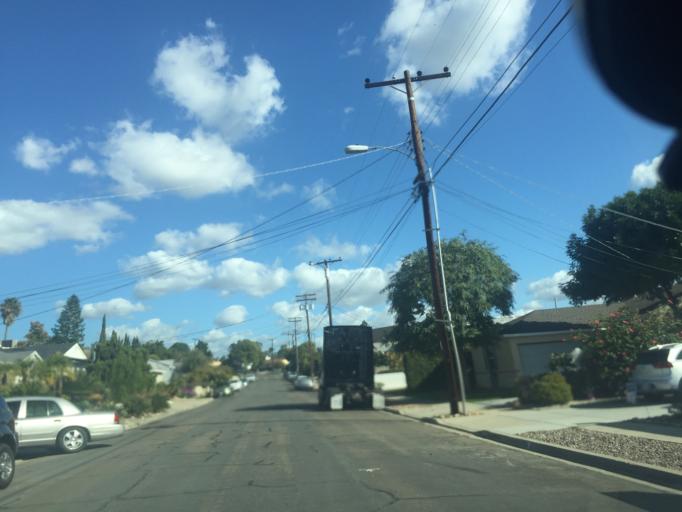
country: US
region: California
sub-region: San Diego County
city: La Mesa
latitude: 32.7846
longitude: -117.0877
